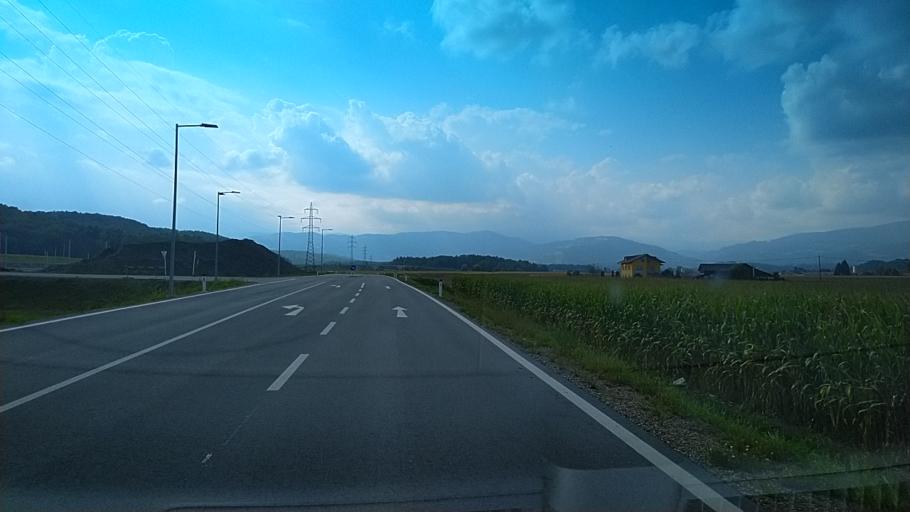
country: AT
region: Styria
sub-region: Politischer Bezirk Deutschlandsberg
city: Gross Sankt Florian
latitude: 46.8152
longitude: 15.3001
